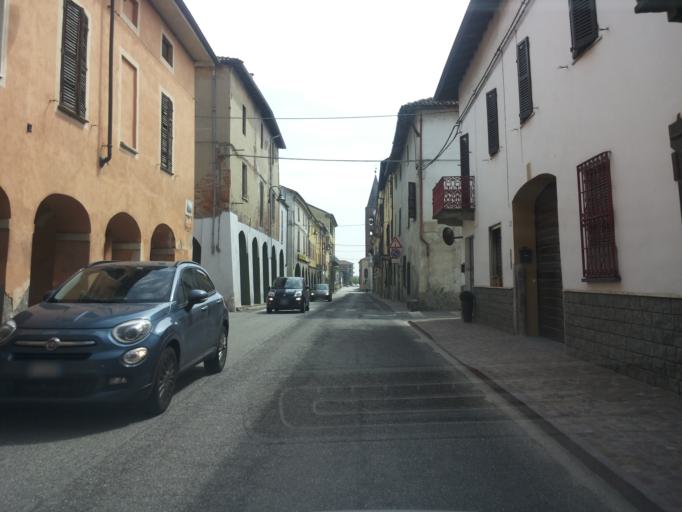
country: IT
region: Piedmont
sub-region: Provincia di Alessandria
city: Occimiano
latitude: 45.0604
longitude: 8.5052
